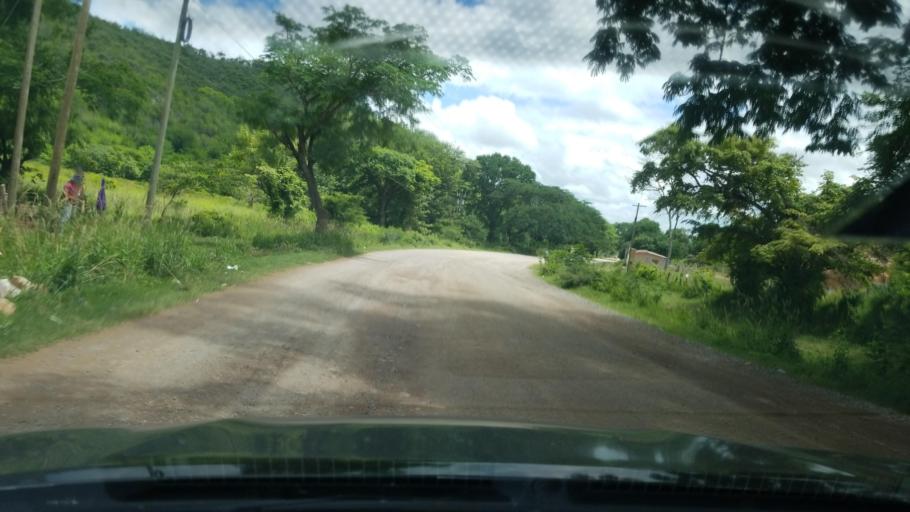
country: HN
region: Francisco Morazan
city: Talanga
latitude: 14.3886
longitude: -87.0746
